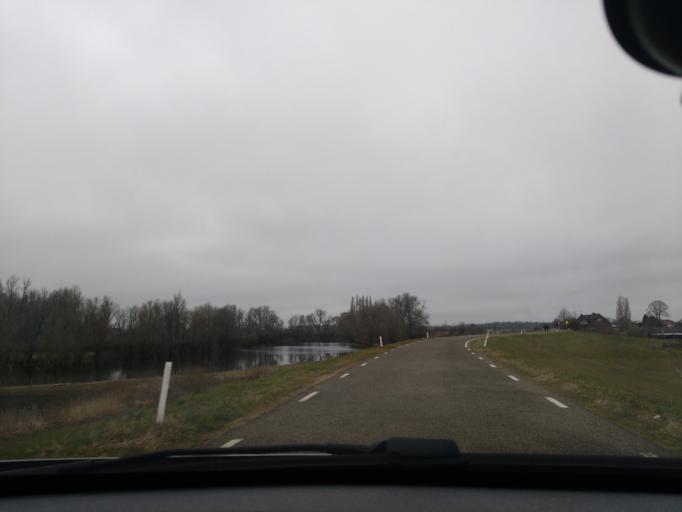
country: NL
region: Gelderland
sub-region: Gemeente Groesbeek
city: Berg en Dal
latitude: 51.8657
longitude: 5.9017
